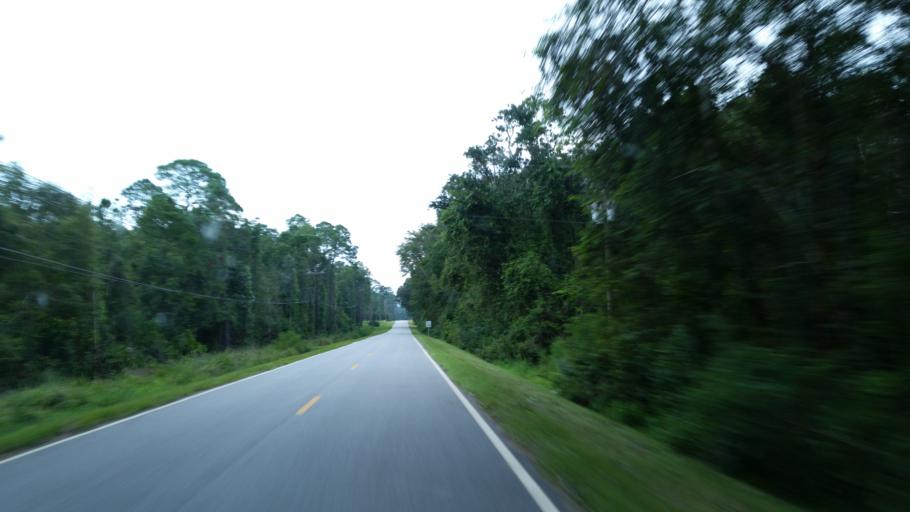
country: US
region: Georgia
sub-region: Lowndes County
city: Valdosta
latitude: 30.7460
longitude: -83.2378
